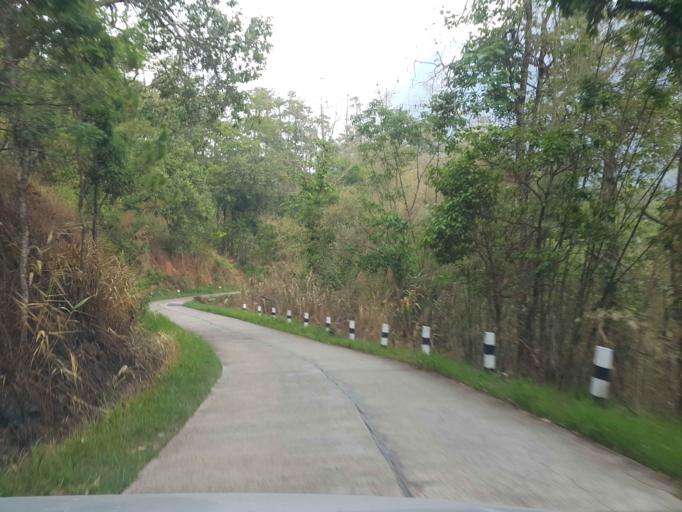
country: TH
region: Chiang Mai
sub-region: Amphoe Chiang Dao
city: Chiang Dao
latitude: 19.4170
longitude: 98.8551
